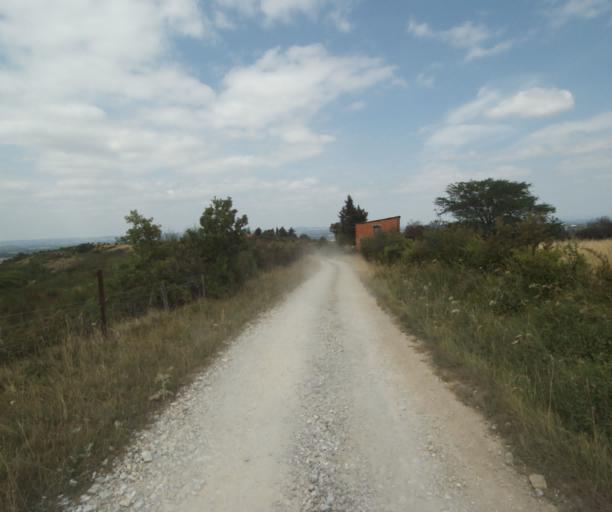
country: FR
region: Midi-Pyrenees
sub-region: Departement du Tarn
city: Soreze
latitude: 43.4403
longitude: 2.0435
